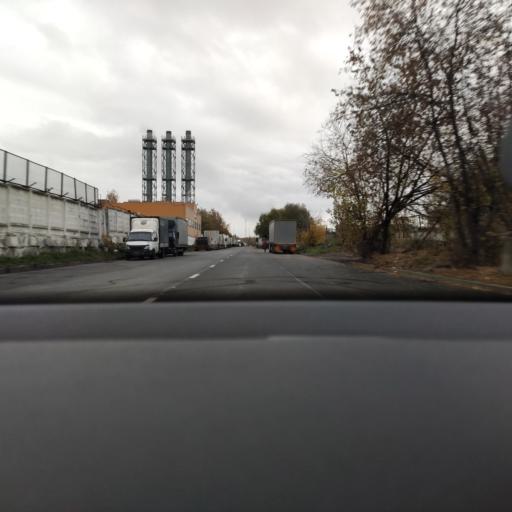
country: RU
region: Moscow
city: Mikhalkovo
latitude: 55.6752
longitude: 37.4292
